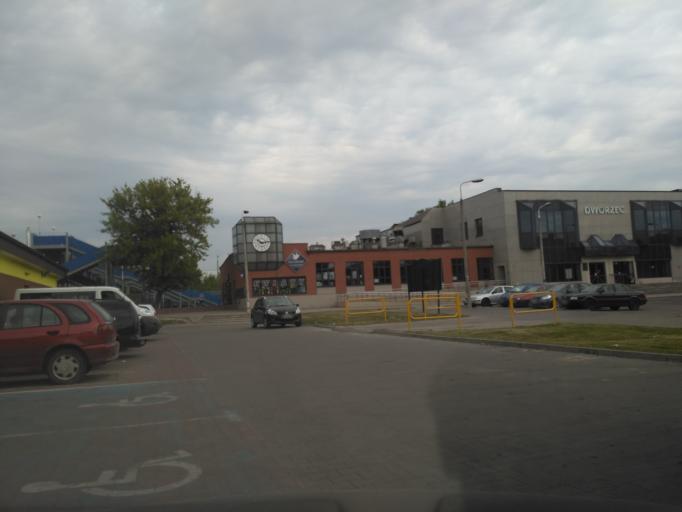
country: PL
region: Lublin Voivodeship
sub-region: Chelm
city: Chelm
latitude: 51.1403
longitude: 23.4935
